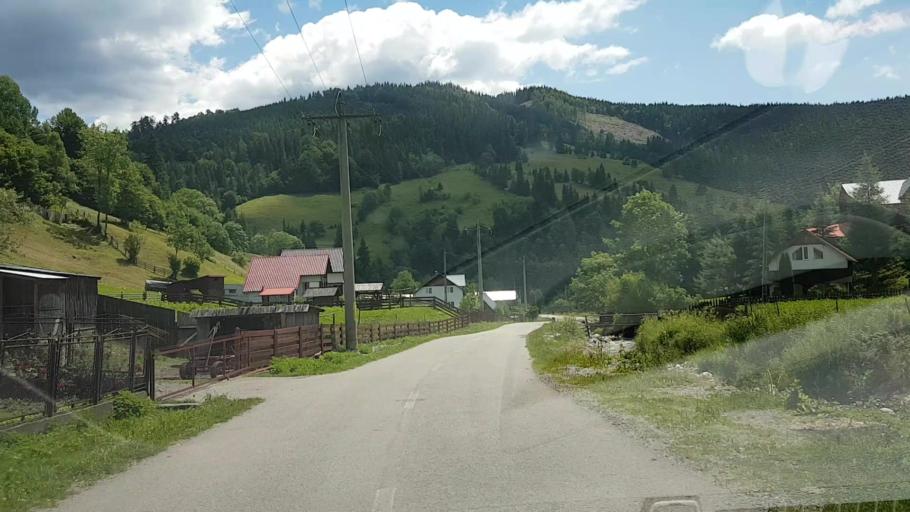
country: RO
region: Suceava
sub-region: Comuna Crucea
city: Crucea
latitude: 47.4185
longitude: 25.5818
